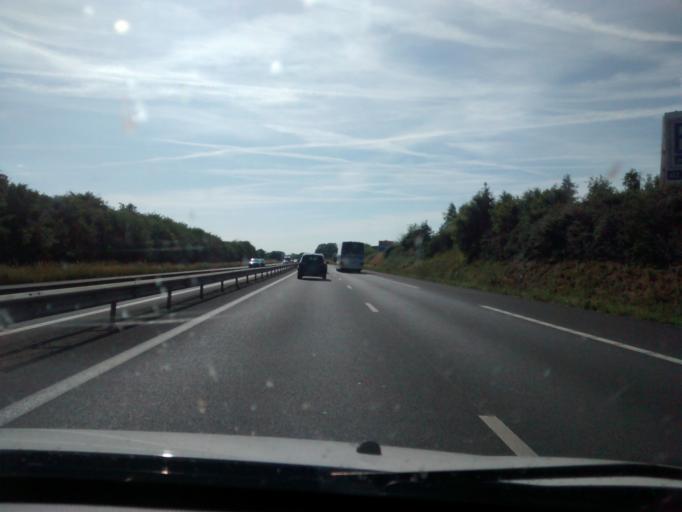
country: FR
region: Brittany
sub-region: Departement d'Ille-et-Vilaine
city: Torce
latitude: 48.0744
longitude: -1.2565
